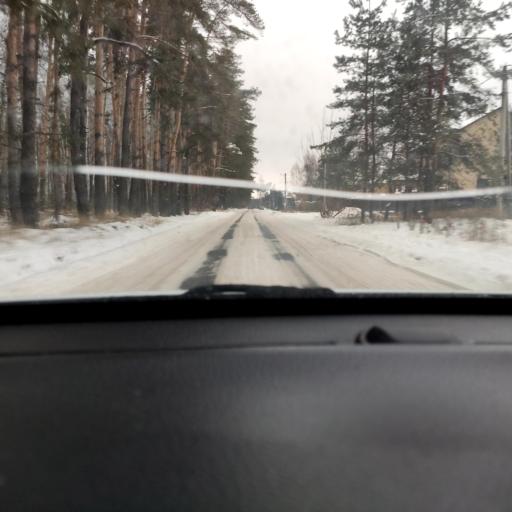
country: RU
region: Voronezj
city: Somovo
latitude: 51.7094
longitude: 39.3225
